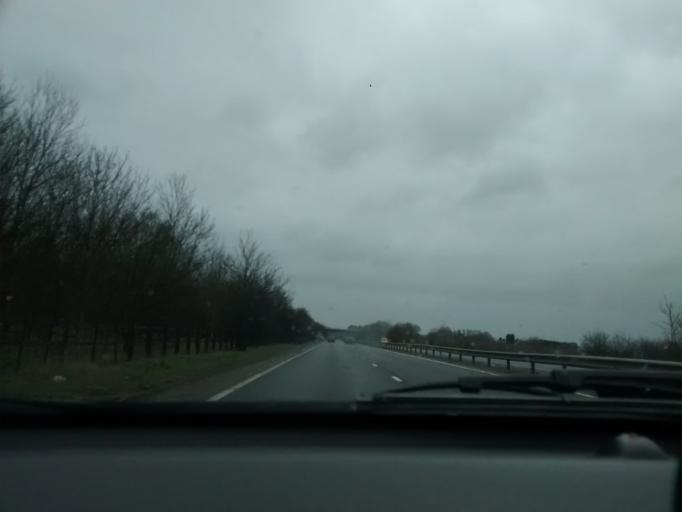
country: GB
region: England
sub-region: Suffolk
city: Needham Market
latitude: 52.1832
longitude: 1.0327
